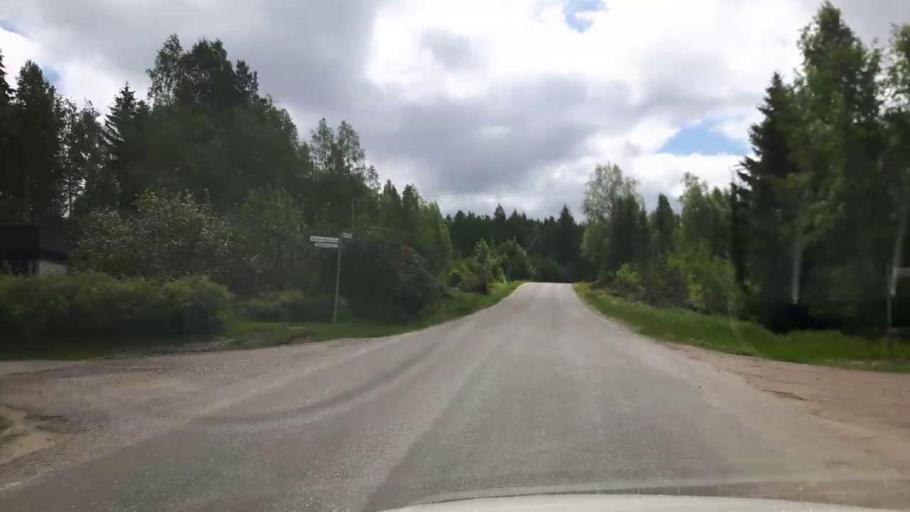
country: SE
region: Gaevleborg
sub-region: Ovanakers Kommun
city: Alfta
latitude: 61.3336
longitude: 15.9685
